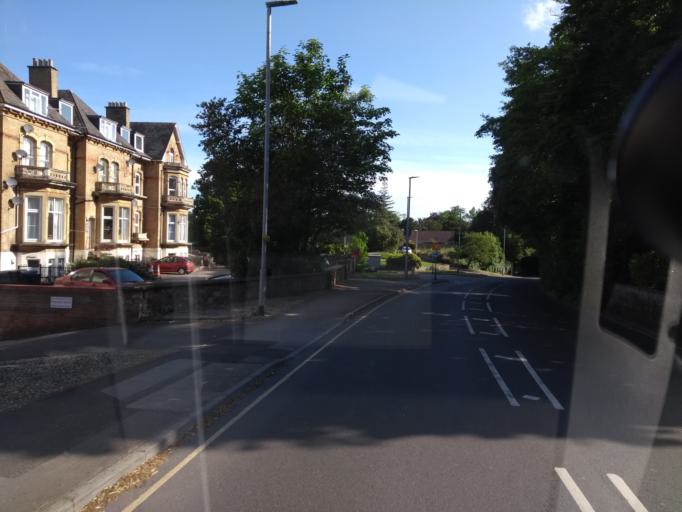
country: GB
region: England
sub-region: Somerset
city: Taunton
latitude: 51.0071
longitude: -3.1123
